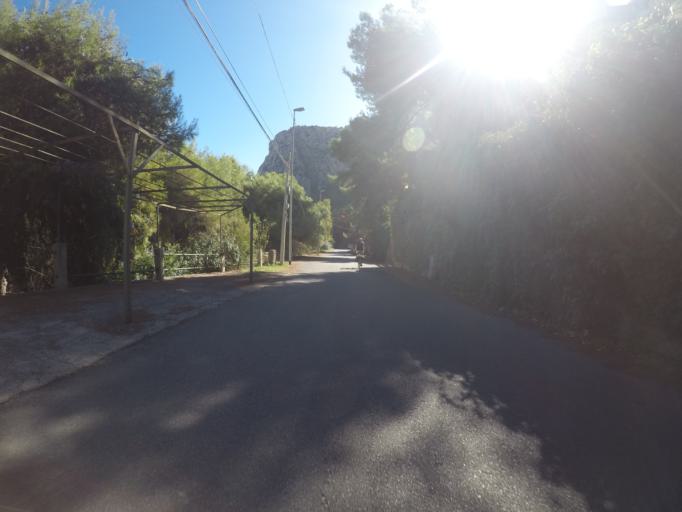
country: IT
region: Sicily
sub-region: Palermo
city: Palermo
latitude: 38.1873
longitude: 13.3445
